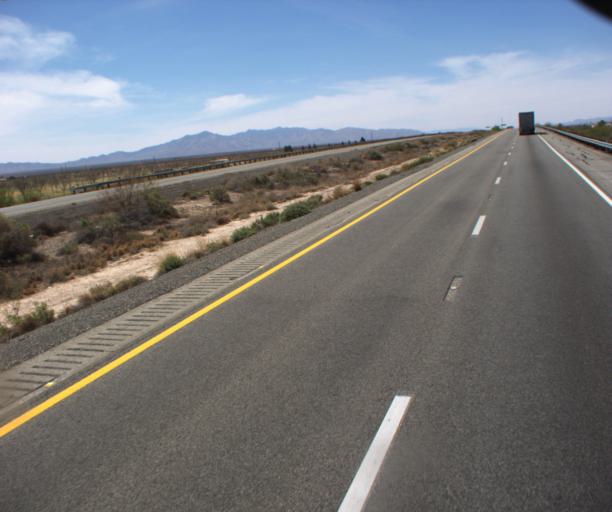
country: US
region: New Mexico
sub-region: Hidalgo County
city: Lordsburg
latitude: 32.2625
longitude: -109.2235
